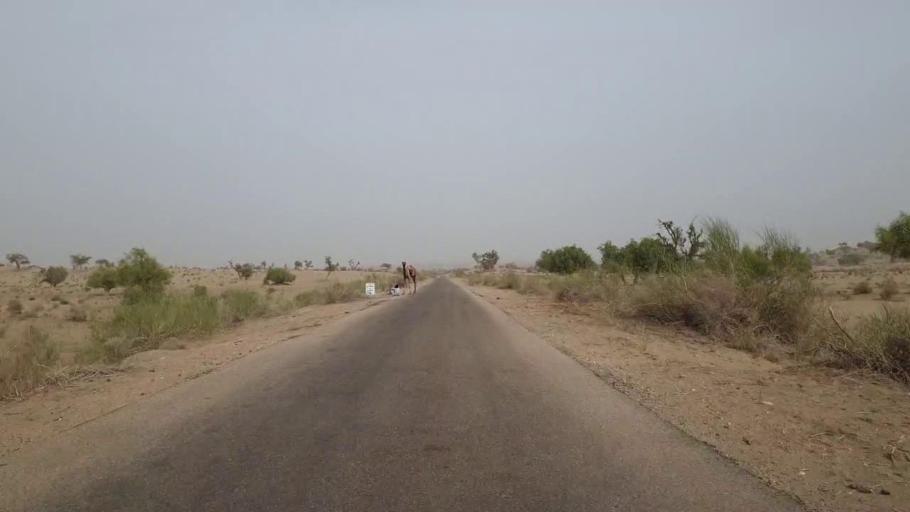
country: PK
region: Sindh
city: Islamkot
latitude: 24.5534
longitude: 70.3513
